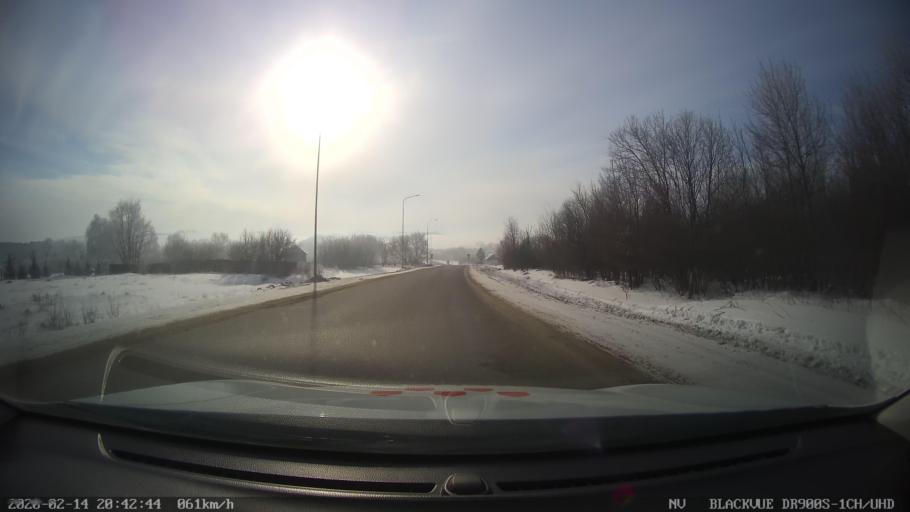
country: RU
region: Tatarstan
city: Kuybyshevskiy Zaton
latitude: 55.3147
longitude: 49.1444
